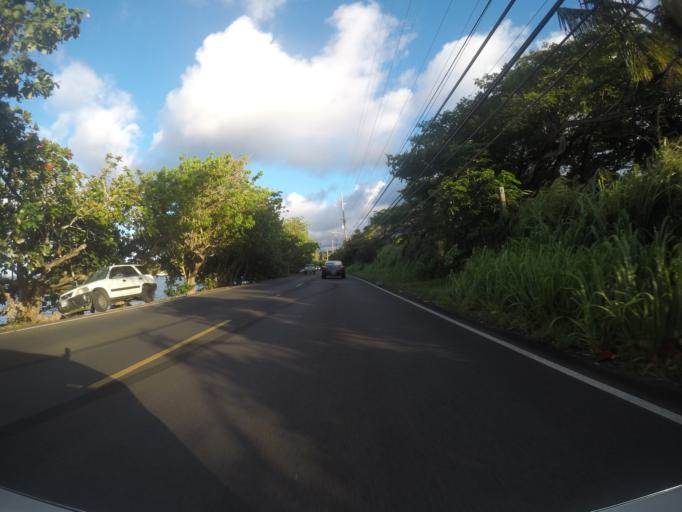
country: US
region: Hawaii
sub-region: Honolulu County
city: He'eia
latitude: 21.4462
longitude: -157.8136
